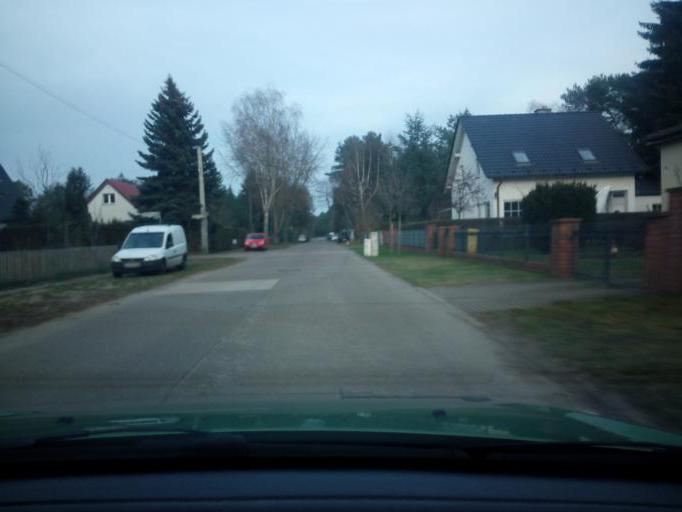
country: DE
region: Berlin
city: Muggelheim
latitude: 52.4116
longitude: 13.6667
